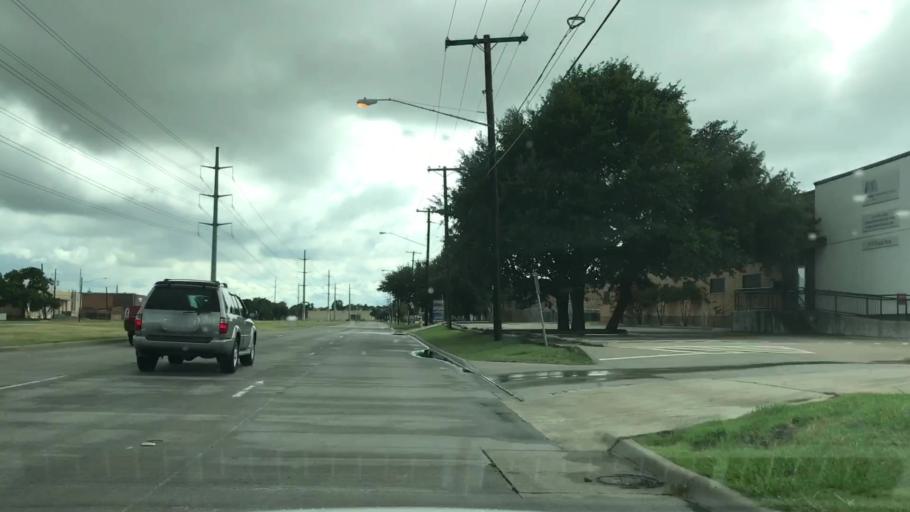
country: US
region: Texas
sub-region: Dallas County
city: Irving
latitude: 32.8197
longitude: -96.8959
